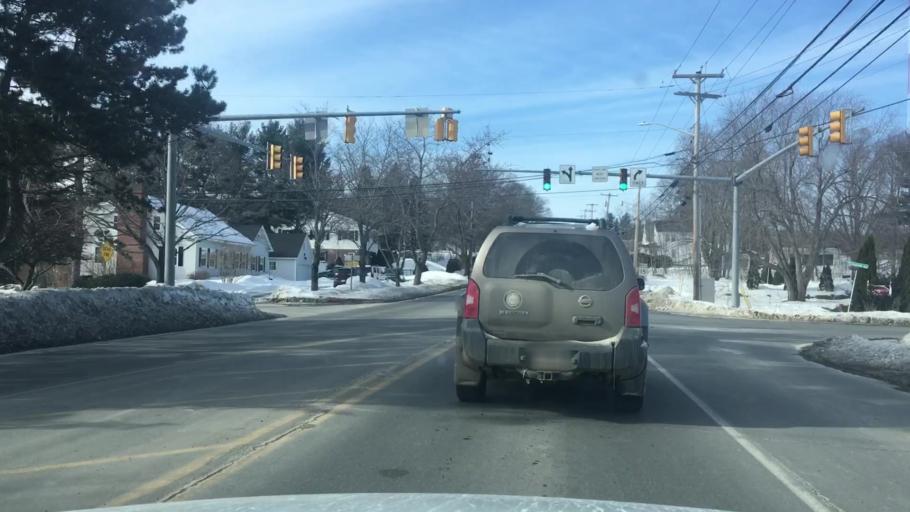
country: US
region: Maine
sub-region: Penobscot County
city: Bangor
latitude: 44.8272
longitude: -68.7828
